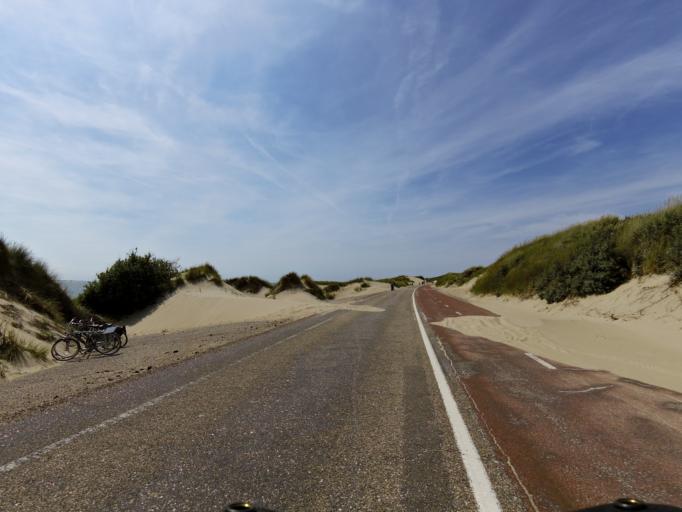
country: NL
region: Zeeland
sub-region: Schouwen-Duiveland
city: Burgh
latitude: 51.6666
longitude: 3.7172
